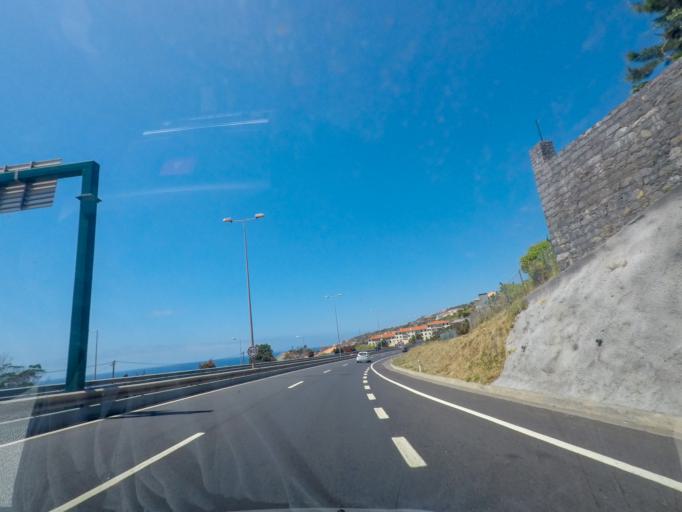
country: PT
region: Madeira
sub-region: Santa Cruz
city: Santa Cruz
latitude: 32.6548
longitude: -16.8150
